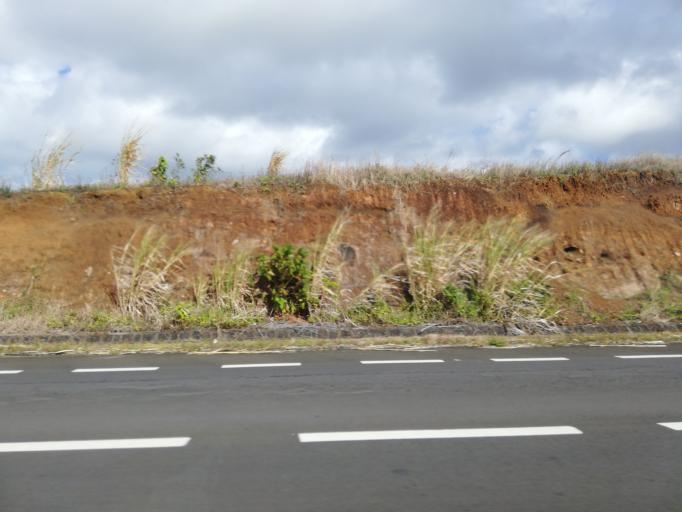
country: MU
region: Grand Port
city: Mahebourg
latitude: -20.4024
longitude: 57.6789
